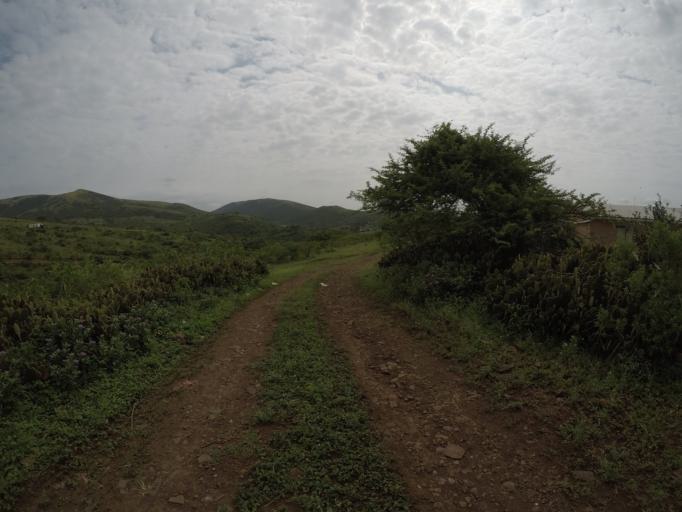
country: ZA
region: KwaZulu-Natal
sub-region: uThungulu District Municipality
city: Empangeni
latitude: -28.6218
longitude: 31.9096
